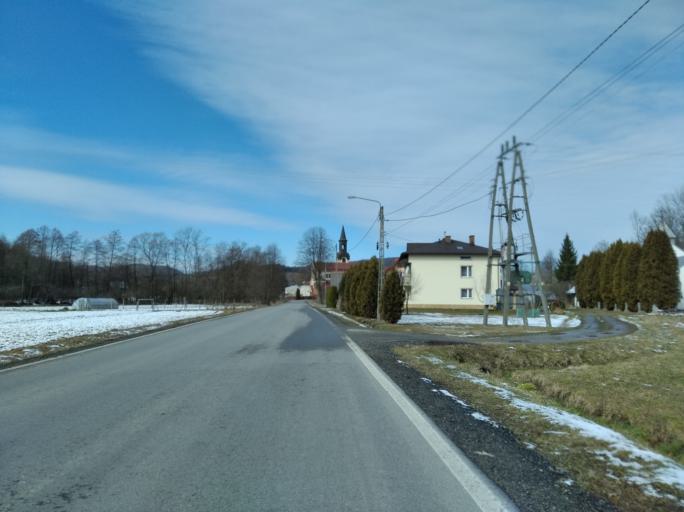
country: PL
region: Subcarpathian Voivodeship
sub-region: Powiat brzozowski
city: Jasienica Rosielna
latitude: 49.7532
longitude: 21.9017
